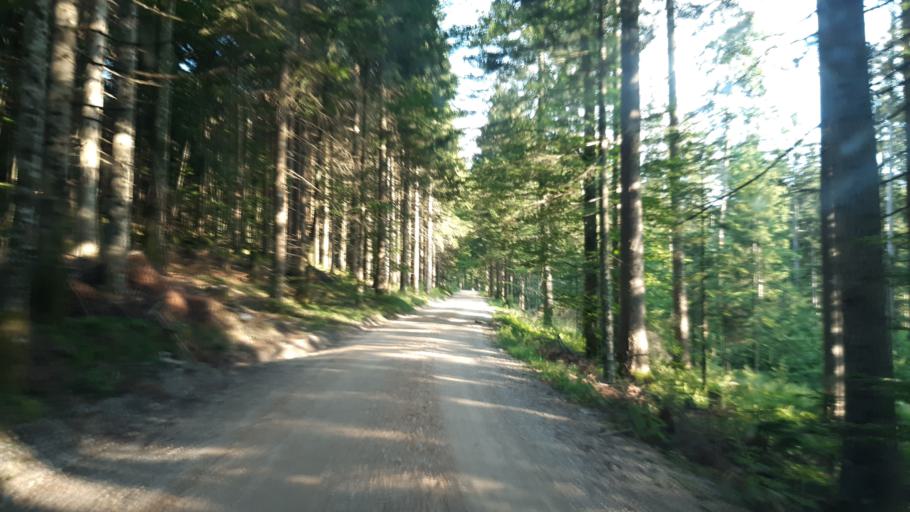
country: SI
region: Dolenjske Toplice
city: Dolenjske Toplice
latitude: 45.7026
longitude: 15.0099
